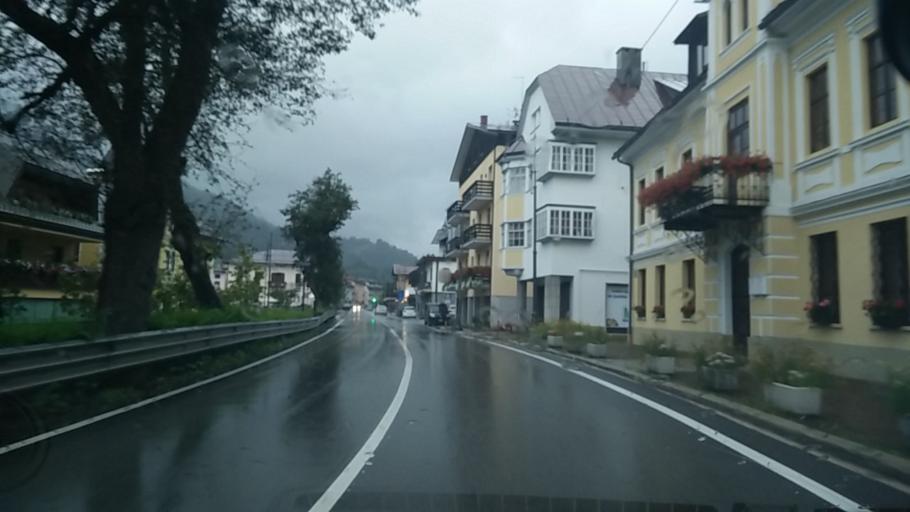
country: IT
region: Friuli Venezia Giulia
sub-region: Provincia di Udine
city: Tarvisio
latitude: 46.5056
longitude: 13.5799
